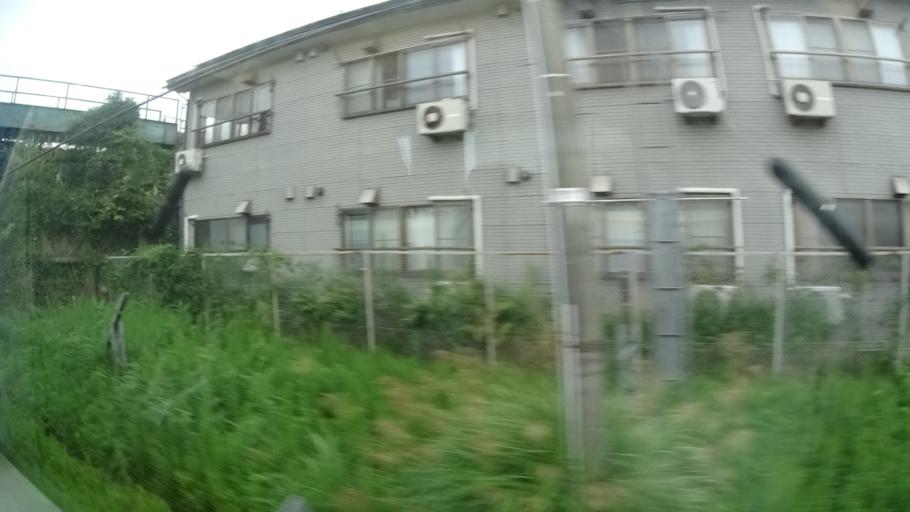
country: JP
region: Yamagata
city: Tsuruoka
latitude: 38.7398
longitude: 139.8420
